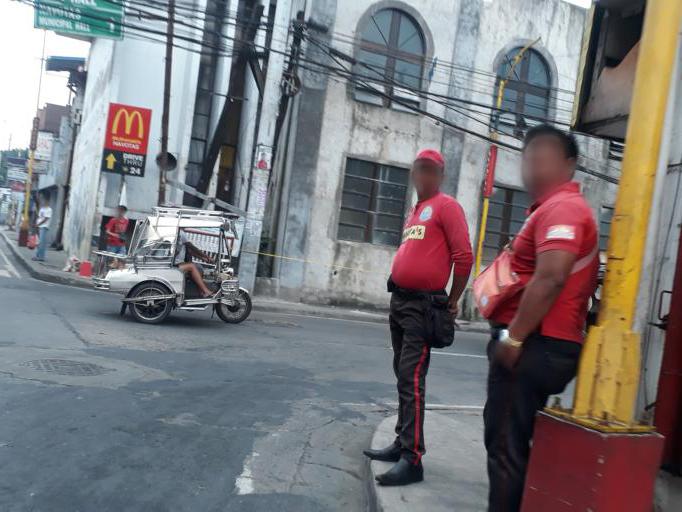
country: PH
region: Metro Manila
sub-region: Caloocan City
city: Niugan
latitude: 14.6546
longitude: 120.9488
